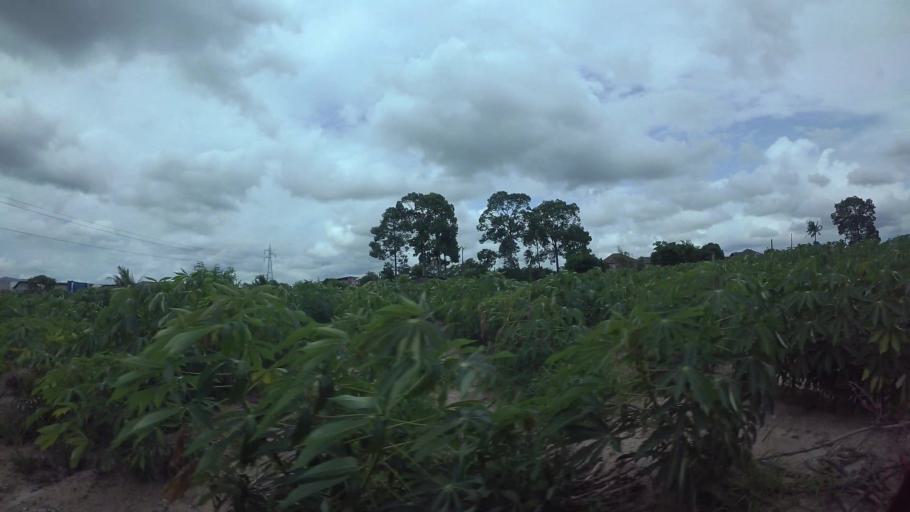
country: TH
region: Chon Buri
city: Si Racha
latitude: 13.1698
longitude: 100.9713
